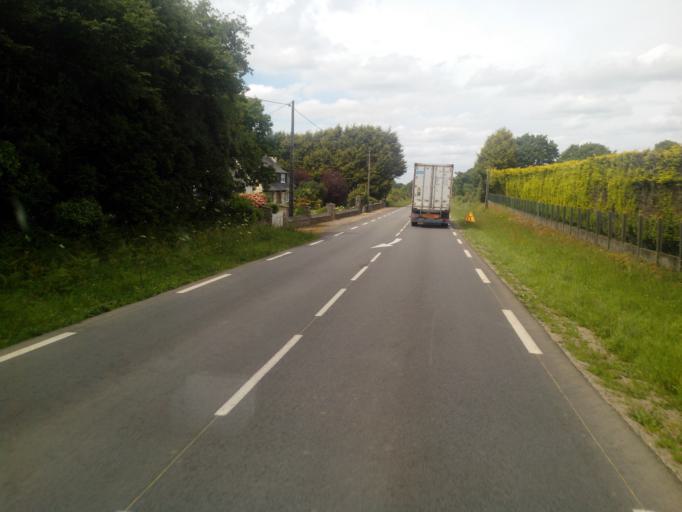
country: FR
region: Brittany
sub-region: Departement du Finistere
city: Guerlesquin
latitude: 48.5554
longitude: -3.5979
